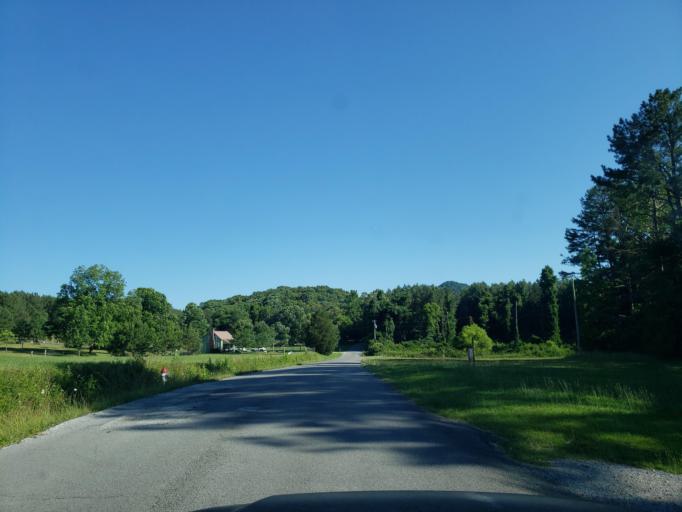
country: US
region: Georgia
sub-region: Whitfield County
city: Dalton
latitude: 34.6592
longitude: -85.0923
